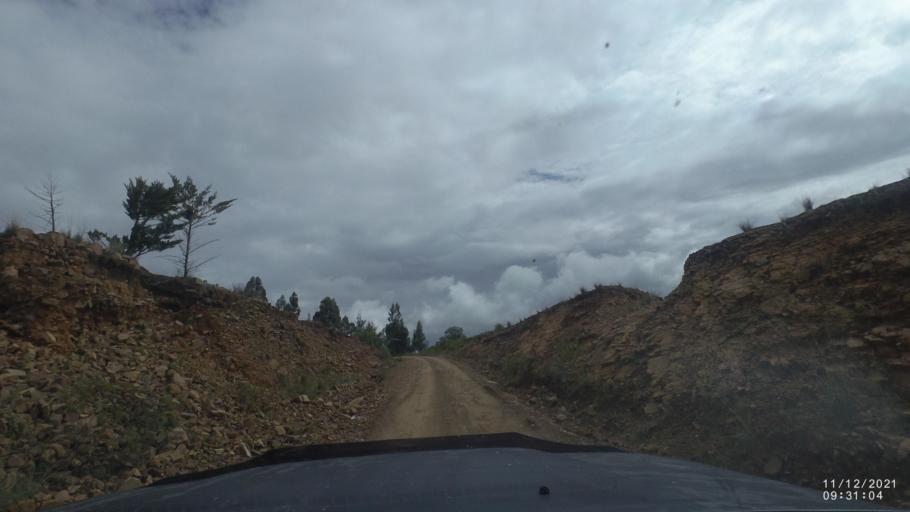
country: BO
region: Cochabamba
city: Tarata
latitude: -17.8553
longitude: -65.9889
